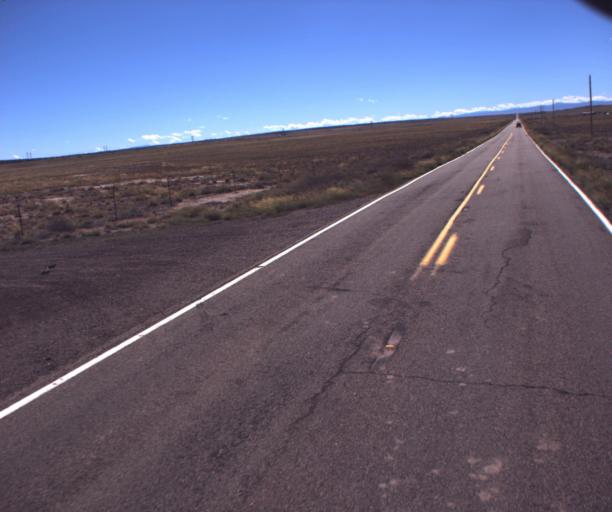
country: US
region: Arizona
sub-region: Apache County
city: Saint Johns
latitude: 34.6057
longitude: -109.3224
